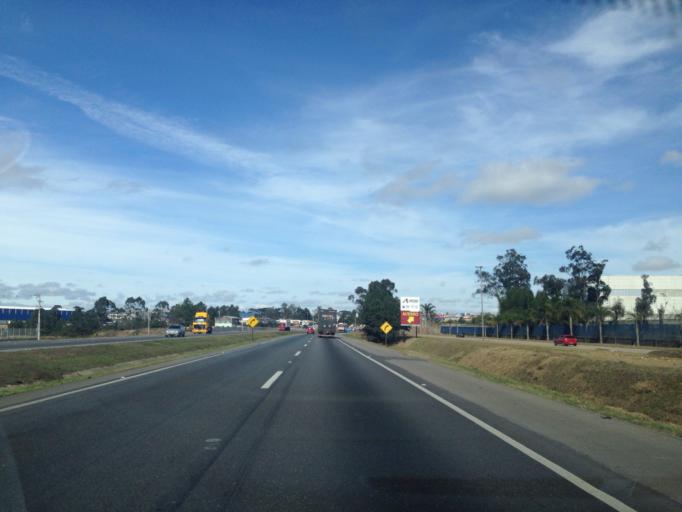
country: BR
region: Parana
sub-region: Sao Jose Dos Pinhais
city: Sao Jose dos Pinhais
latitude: -25.5529
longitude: -49.1500
